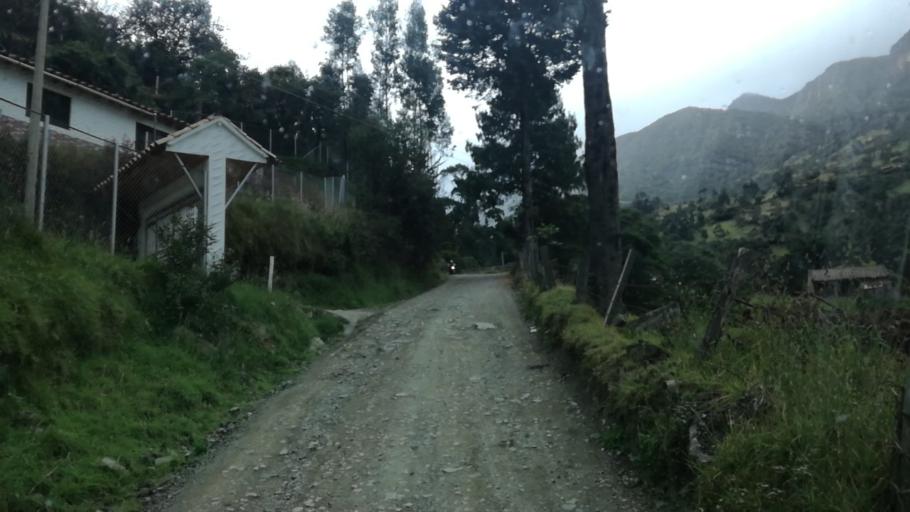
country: CO
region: Boyaca
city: Socha Viejo
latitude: 5.9428
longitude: -72.6876
